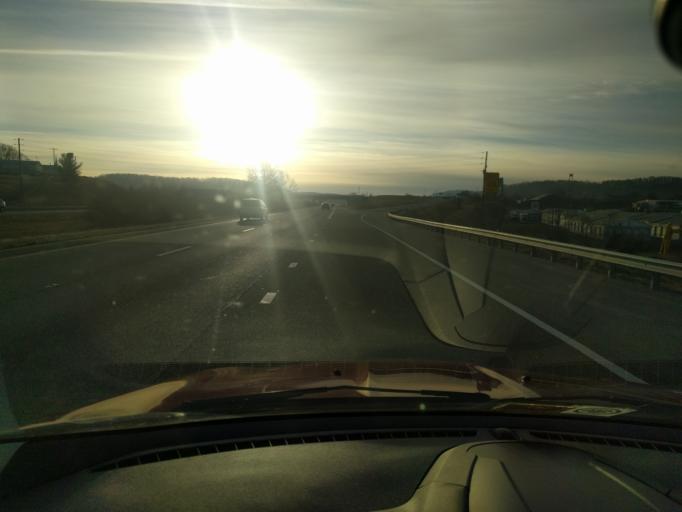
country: US
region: Virginia
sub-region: Augusta County
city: Fishersville
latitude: 38.0862
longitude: -78.9929
